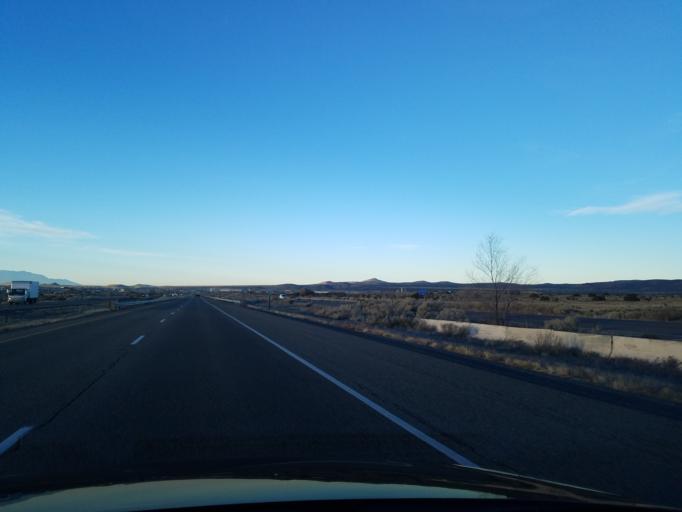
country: US
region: New Mexico
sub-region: Santa Fe County
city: Agua Fria
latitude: 35.6469
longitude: -106.0558
